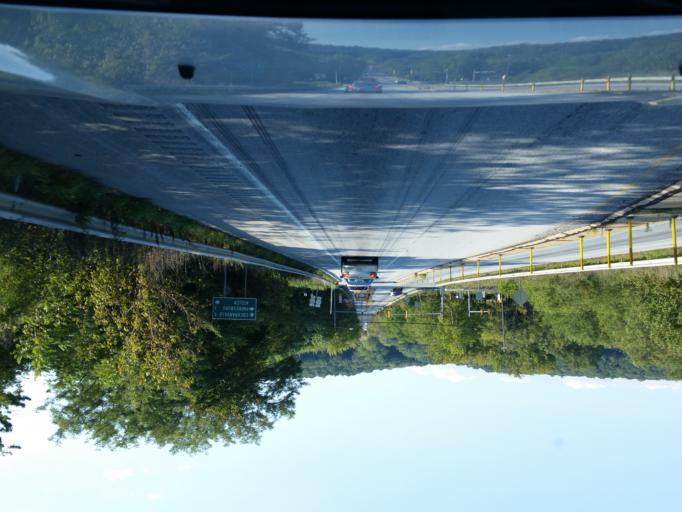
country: US
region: Pennsylvania
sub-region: Chester County
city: Atglen
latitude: 39.9485
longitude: -75.9697
